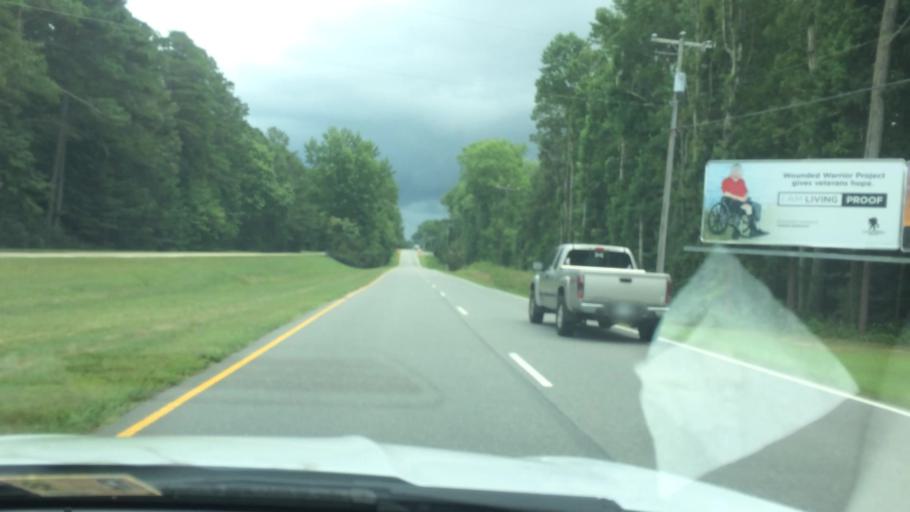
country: US
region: Virginia
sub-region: King William County
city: West Point
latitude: 37.4036
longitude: -76.8318
